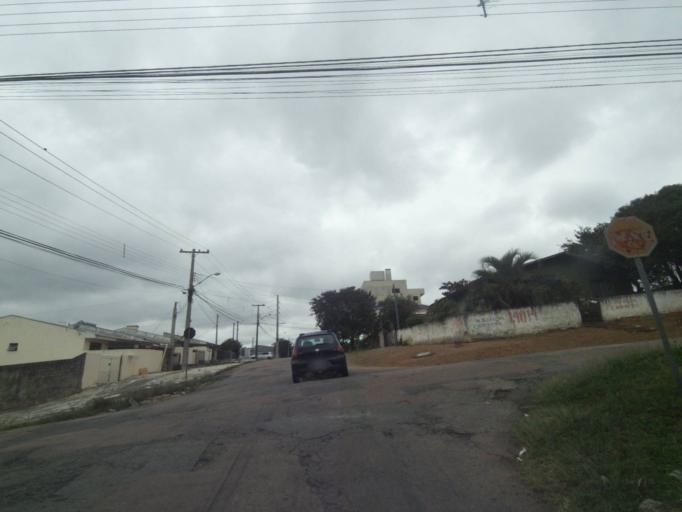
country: BR
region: Parana
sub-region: Sao Jose Dos Pinhais
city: Sao Jose dos Pinhais
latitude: -25.5430
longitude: -49.2852
